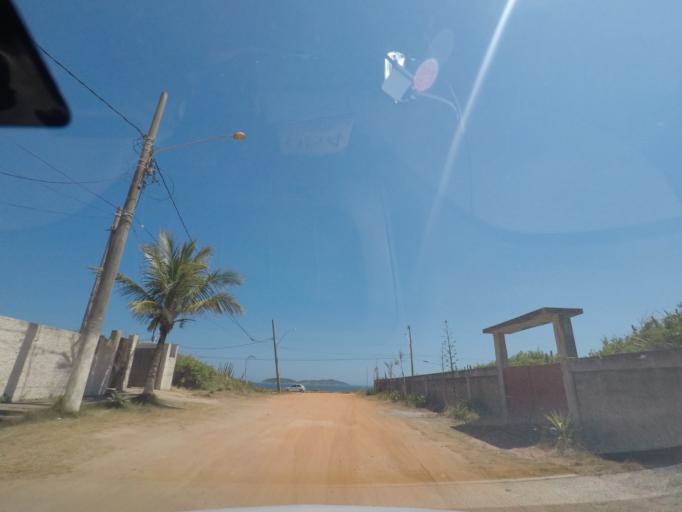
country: BR
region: Rio de Janeiro
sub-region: Marica
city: Marica
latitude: -22.9737
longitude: -42.9207
